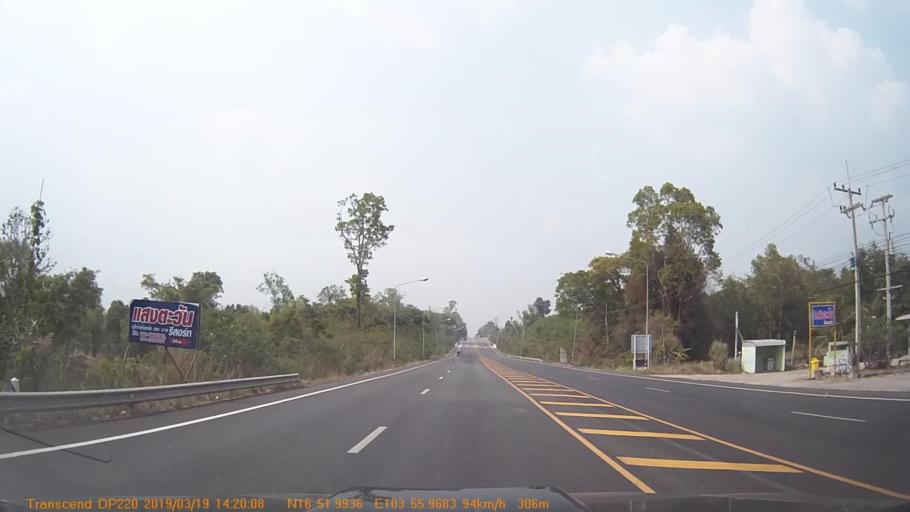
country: TH
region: Sakon Nakhon
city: Phu Phan
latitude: 16.8672
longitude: 103.9327
